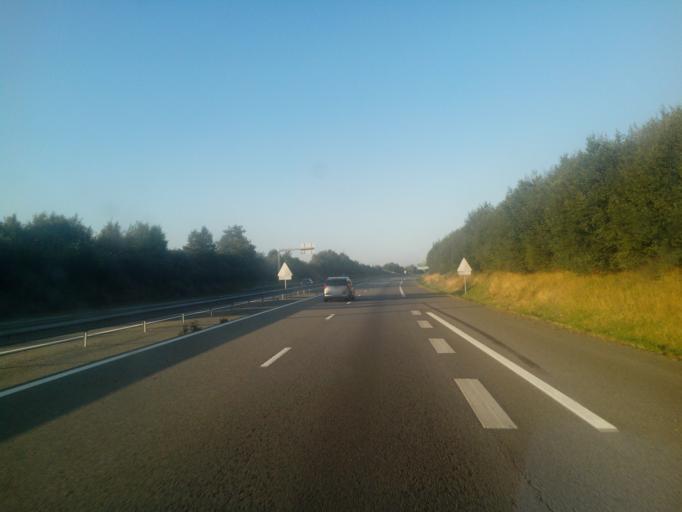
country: FR
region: Brittany
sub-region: Departement du Morbihan
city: Saint-Gonnery
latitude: 48.1234
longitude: -2.8484
